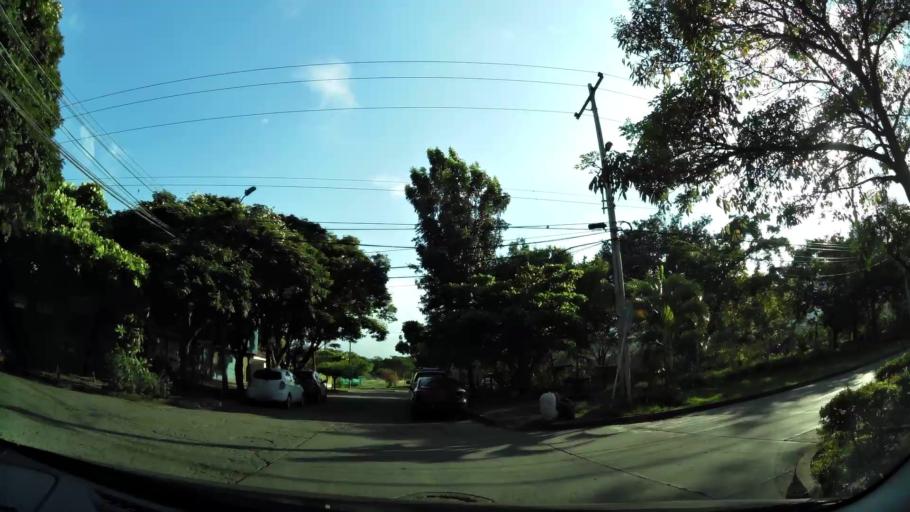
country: CO
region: Valle del Cauca
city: Cali
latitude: 3.4187
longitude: -76.5511
